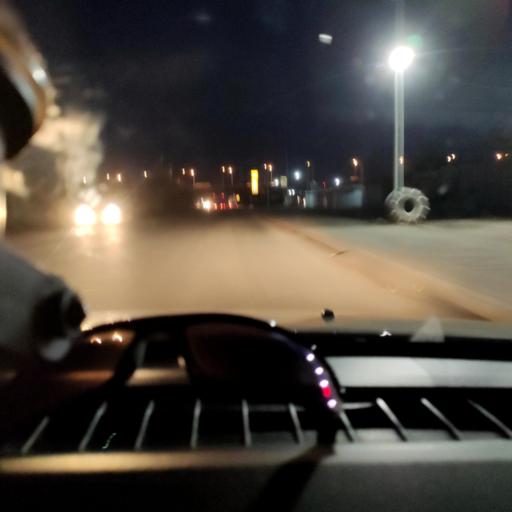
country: RU
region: Samara
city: Samara
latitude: 53.1766
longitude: 50.1981
